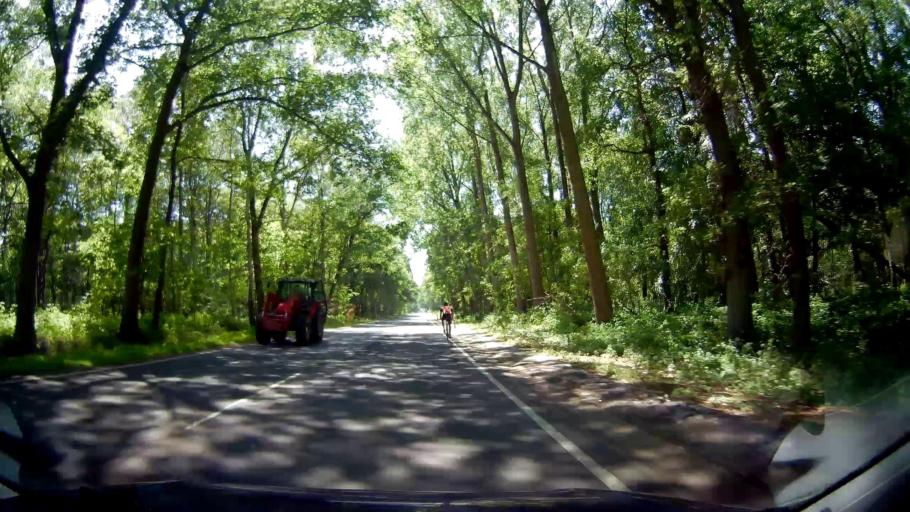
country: DE
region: North Rhine-Westphalia
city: Marl
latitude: 51.6418
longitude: 7.0453
